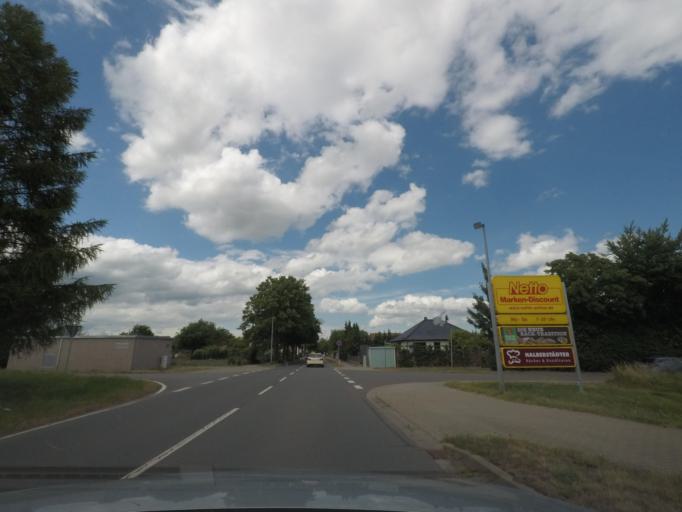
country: DE
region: Saxony-Anhalt
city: Schwanebeck
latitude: 51.9617
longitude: 11.1215
